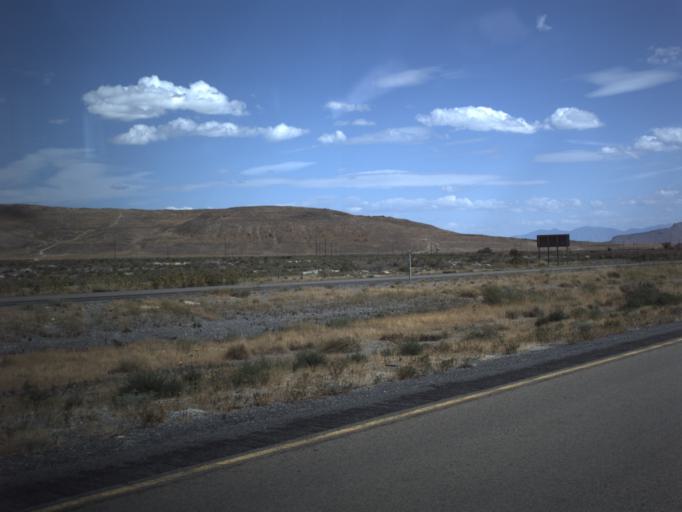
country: US
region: Utah
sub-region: Tooele County
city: Grantsville
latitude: 40.7729
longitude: -112.8001
